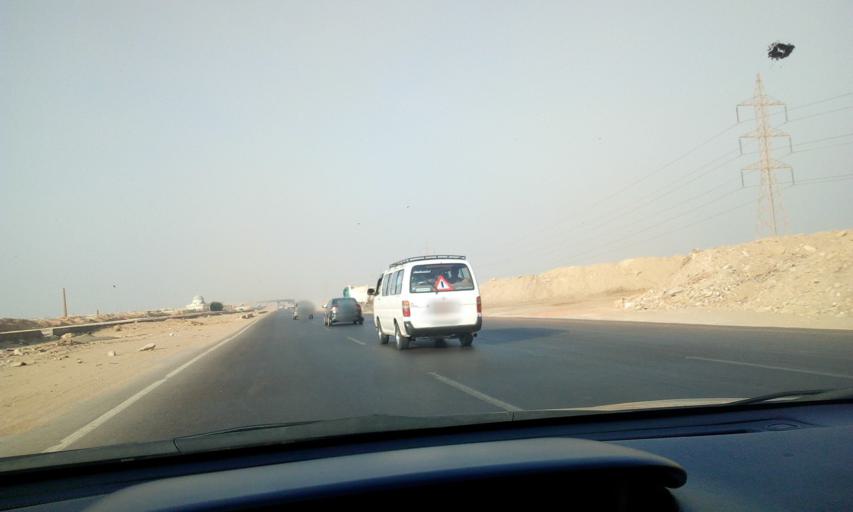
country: EG
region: Al Jizah
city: Madinat Sittah Uktubar
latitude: 29.9135
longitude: 31.0912
